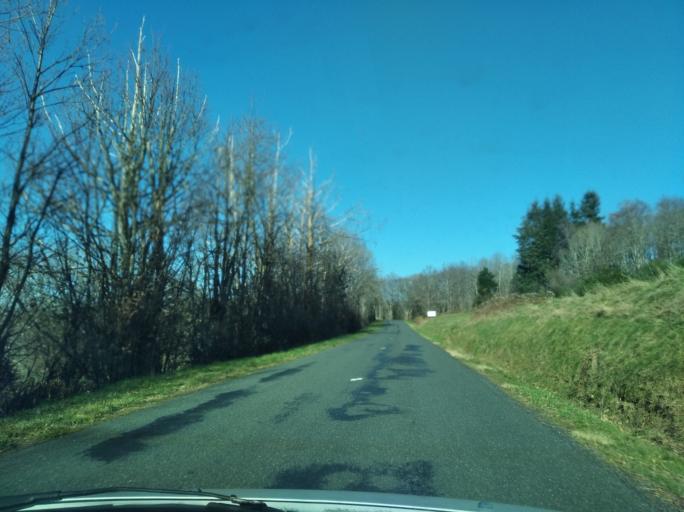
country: FR
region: Auvergne
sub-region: Departement de l'Allier
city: Le Mayet-de-Montagne
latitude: 46.1043
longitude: 3.7588
